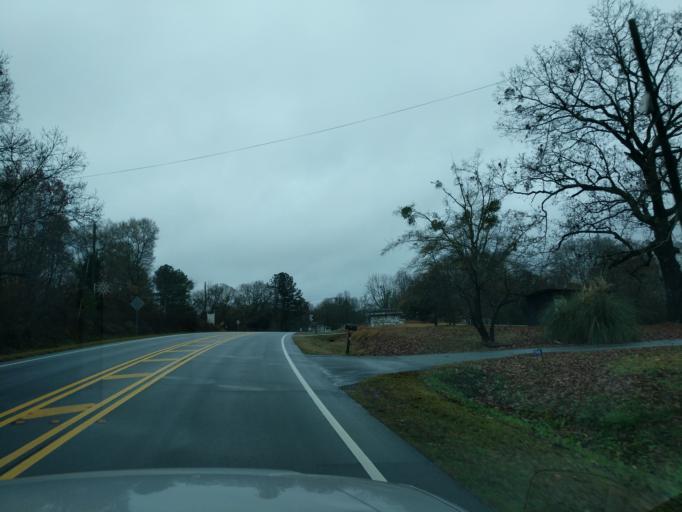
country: US
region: Georgia
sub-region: Franklin County
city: Lavonia
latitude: 34.3757
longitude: -83.0855
